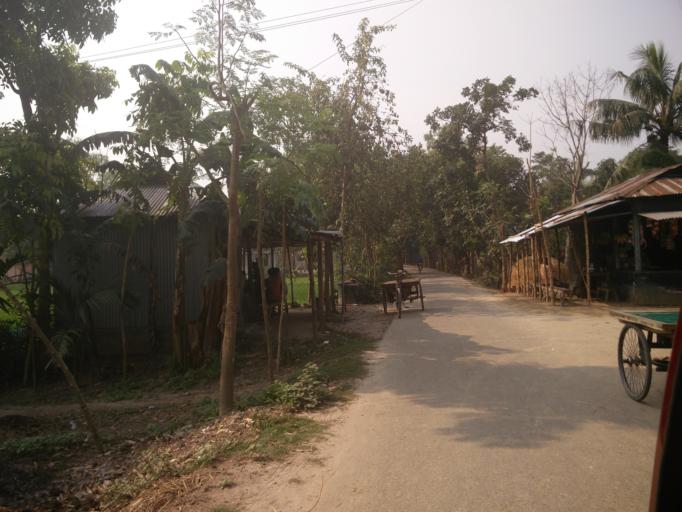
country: BD
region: Dhaka
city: Sherpur
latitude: 24.9131
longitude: 90.1562
